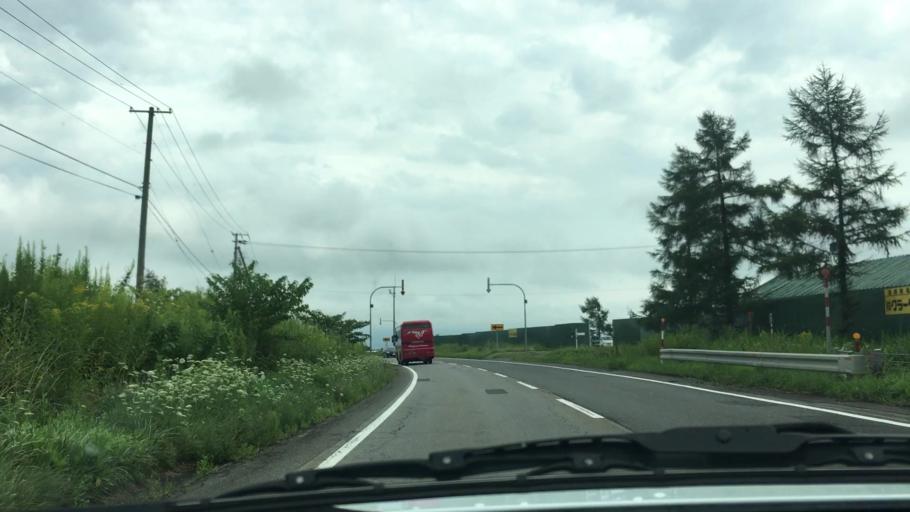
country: JP
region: Hokkaido
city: Chitose
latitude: 42.9427
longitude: 141.7590
